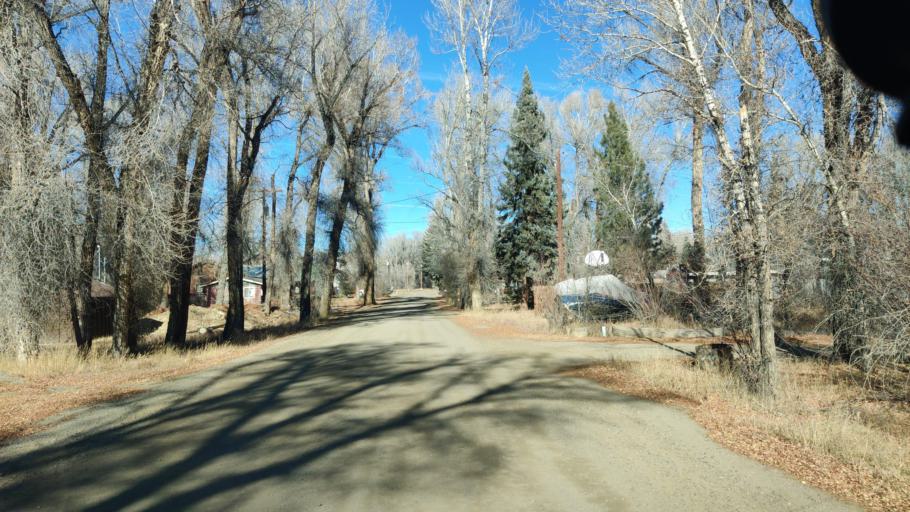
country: US
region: Colorado
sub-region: Gunnison County
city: Gunnison
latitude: 38.5342
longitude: -106.9500
